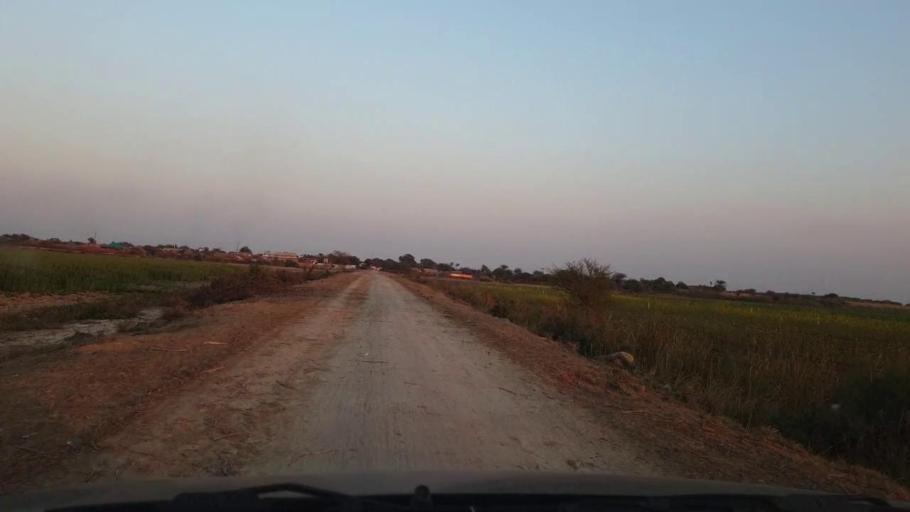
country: PK
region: Sindh
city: Jhol
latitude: 25.9299
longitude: 68.9718
